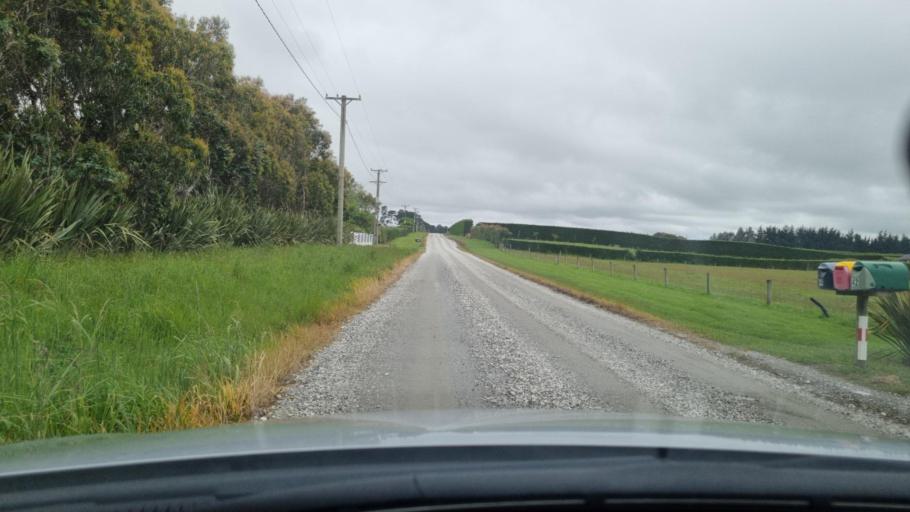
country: NZ
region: Southland
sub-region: Invercargill City
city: Invercargill
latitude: -46.4121
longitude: 168.4408
